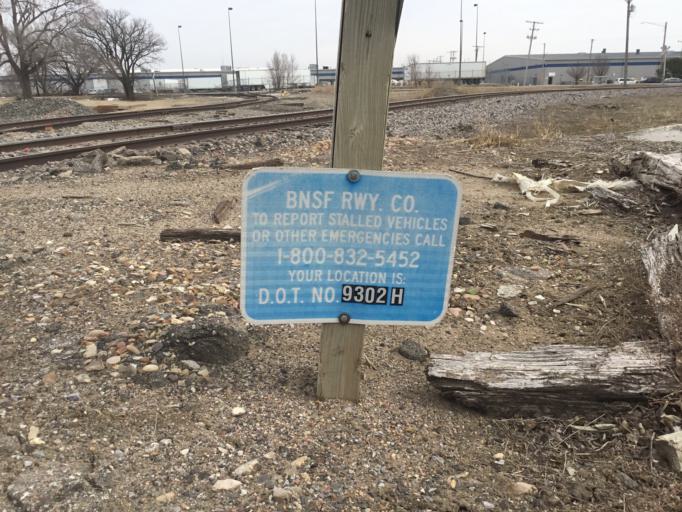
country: US
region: Kansas
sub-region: Sedgwick County
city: Wichita
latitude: 37.7452
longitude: -97.3318
